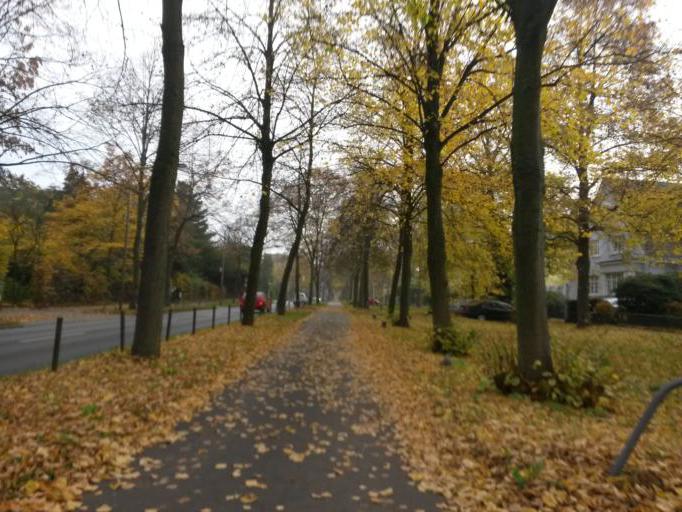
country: DE
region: Bremen
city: Bremen
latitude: 53.0920
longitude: 8.8336
